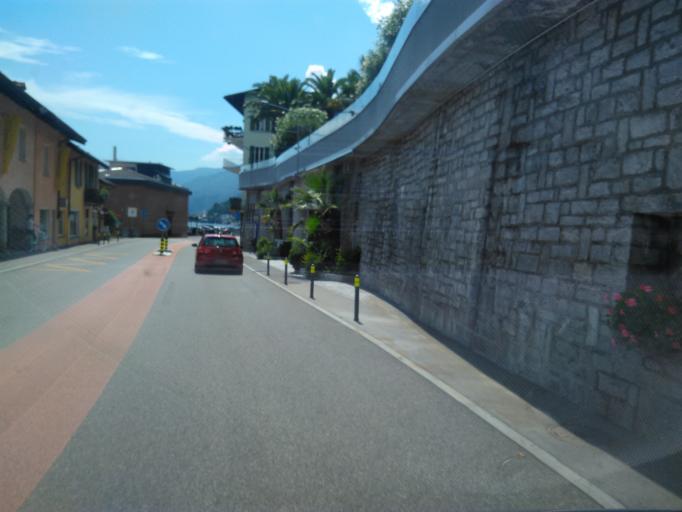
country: CH
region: Ticino
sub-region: Locarno District
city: Brissago
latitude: 46.1407
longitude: 8.7265
